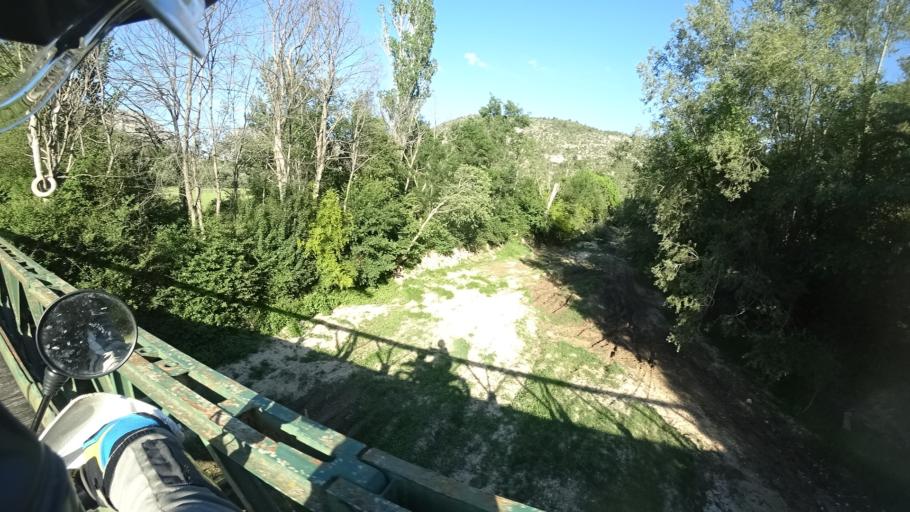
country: HR
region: Sibensko-Kniniska
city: Drnis
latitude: 43.8265
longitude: 16.0222
